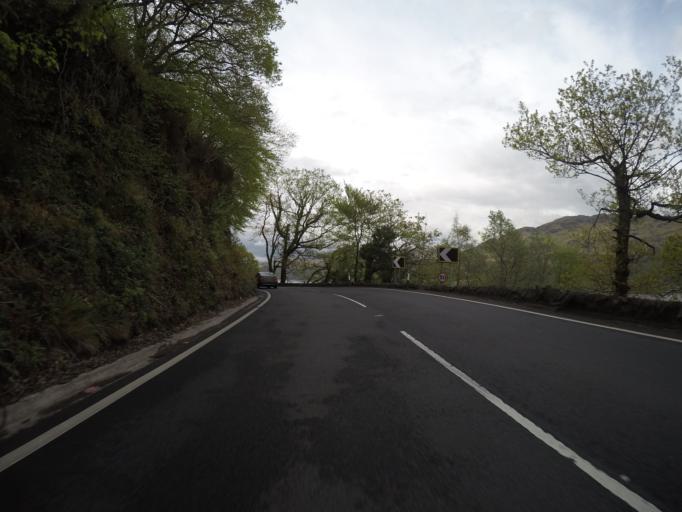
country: GB
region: Scotland
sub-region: Argyll and Bute
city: Garelochhead
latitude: 56.2222
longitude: -4.6957
